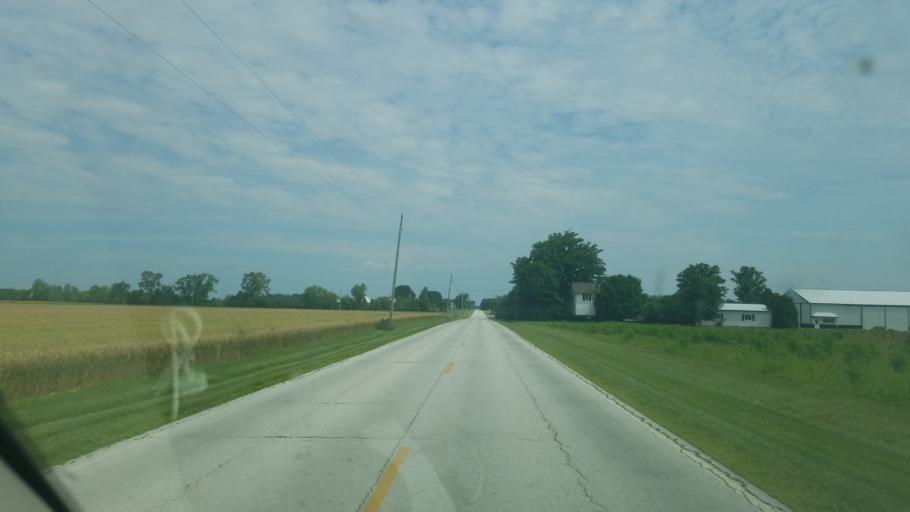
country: US
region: Ohio
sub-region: Seneca County
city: Fostoria
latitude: 41.0906
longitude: -83.4784
